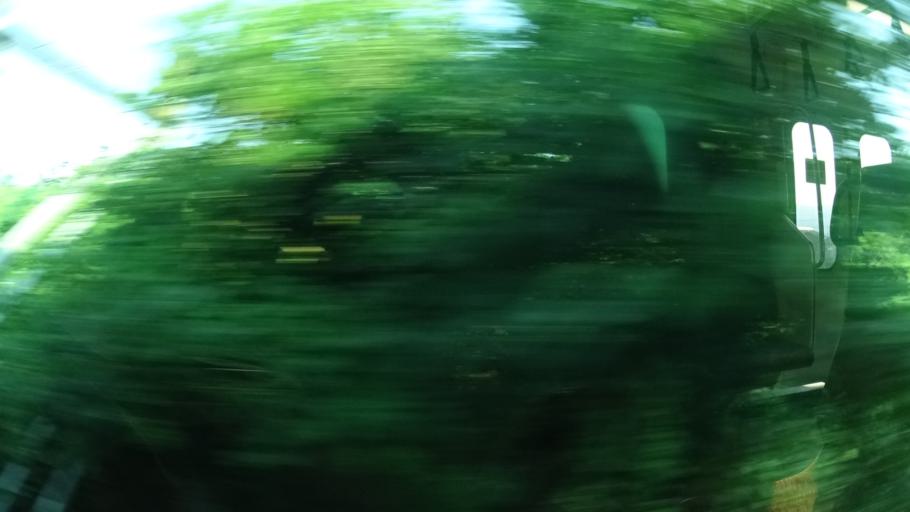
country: JP
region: Ibaraki
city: Takahagi
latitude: 36.6810
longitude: 140.6940
